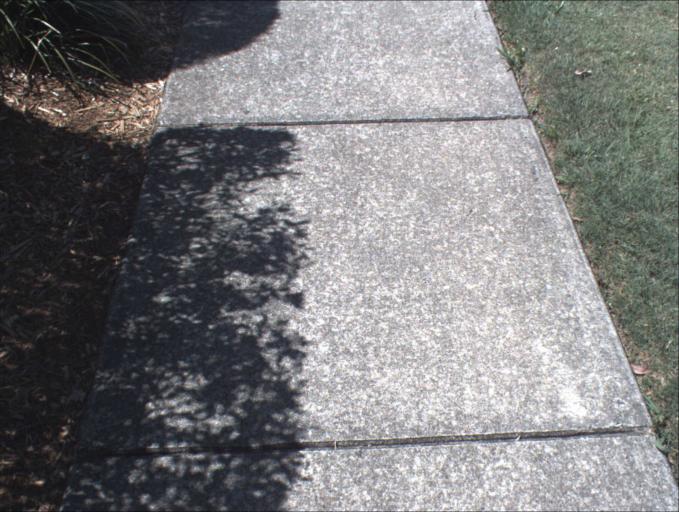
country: AU
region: Queensland
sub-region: Logan
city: Beenleigh
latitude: -27.6884
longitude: 153.2156
